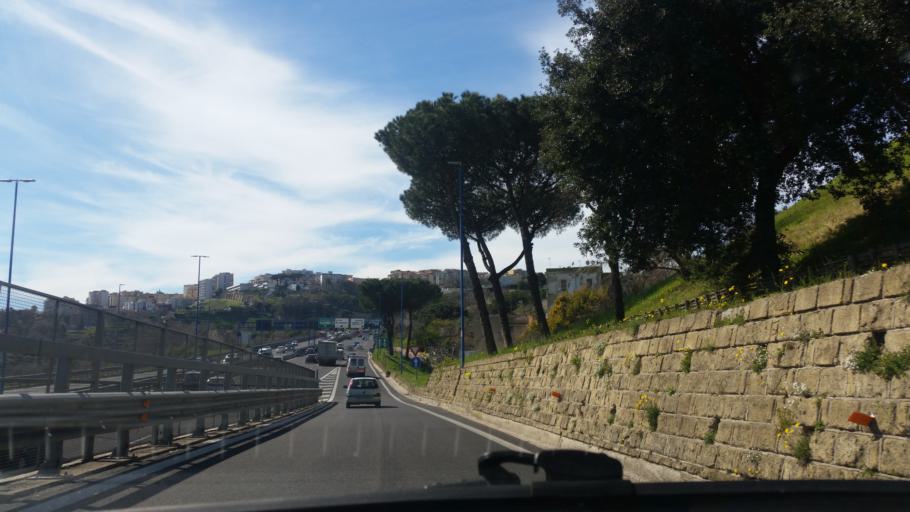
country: IT
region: Campania
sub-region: Provincia di Napoli
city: Napoli
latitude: 40.8647
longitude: 14.2404
